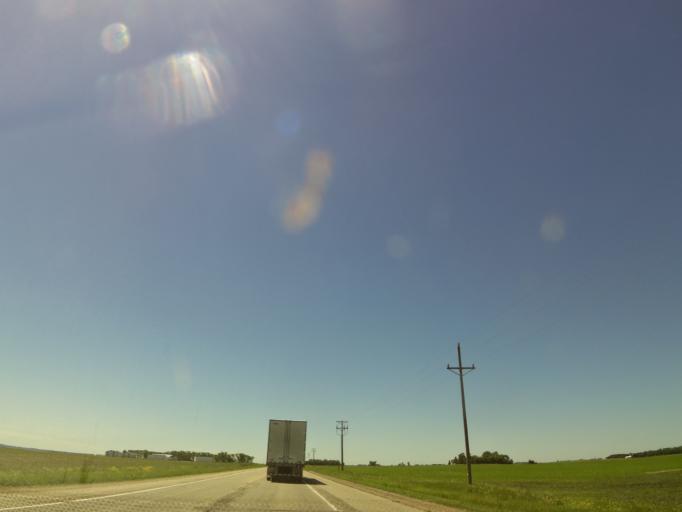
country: US
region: Minnesota
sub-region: Mahnomen County
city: Mahnomen
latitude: 47.2638
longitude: -95.9333
